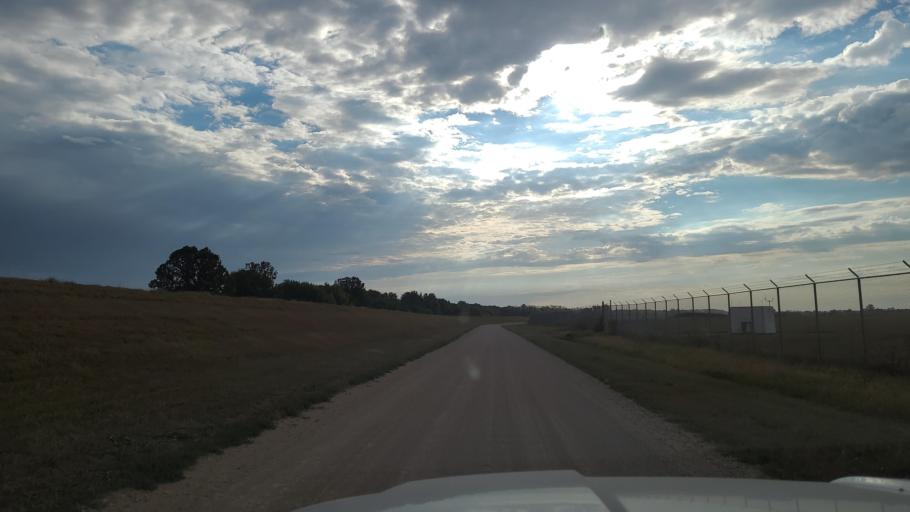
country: US
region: Kansas
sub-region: Douglas County
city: Lawrence
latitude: 39.0222
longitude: -95.2215
